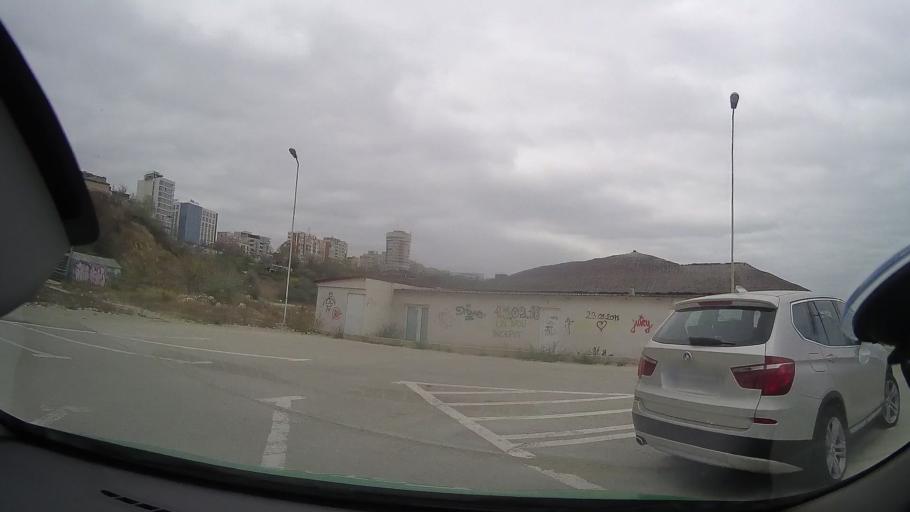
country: RO
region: Constanta
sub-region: Municipiul Constanta
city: Constanta
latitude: 44.1776
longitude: 28.6588
